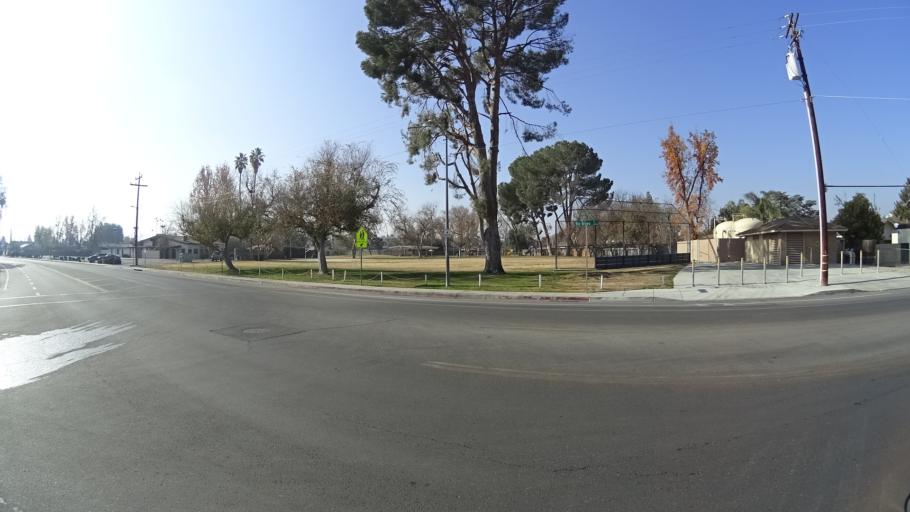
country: US
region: California
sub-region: Kern County
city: Greenacres
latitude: 35.3577
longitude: -119.0688
